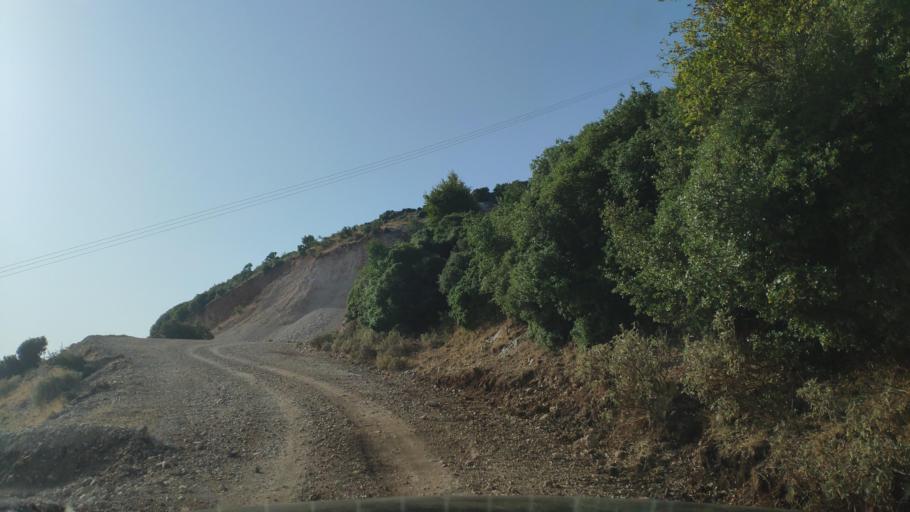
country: GR
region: West Greece
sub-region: Nomos Aitolias kai Akarnanias
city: Monastirakion
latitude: 38.8393
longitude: 20.9741
